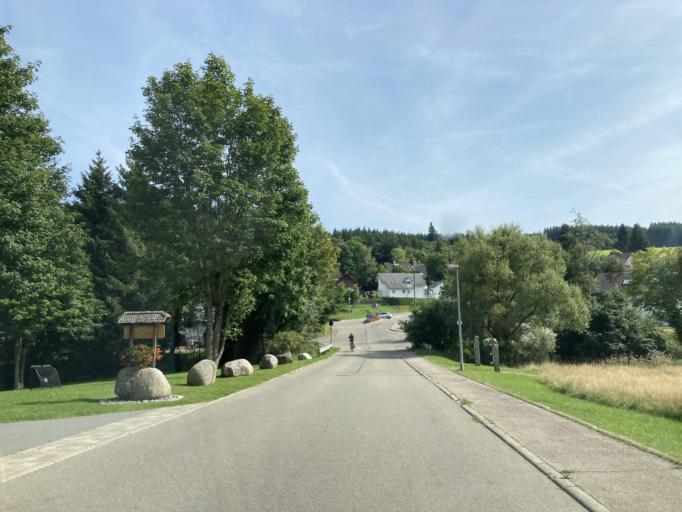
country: DE
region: Baden-Wuerttemberg
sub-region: Freiburg Region
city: Sankt Georgen im Schwarzwald
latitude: 48.1148
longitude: 8.3082
